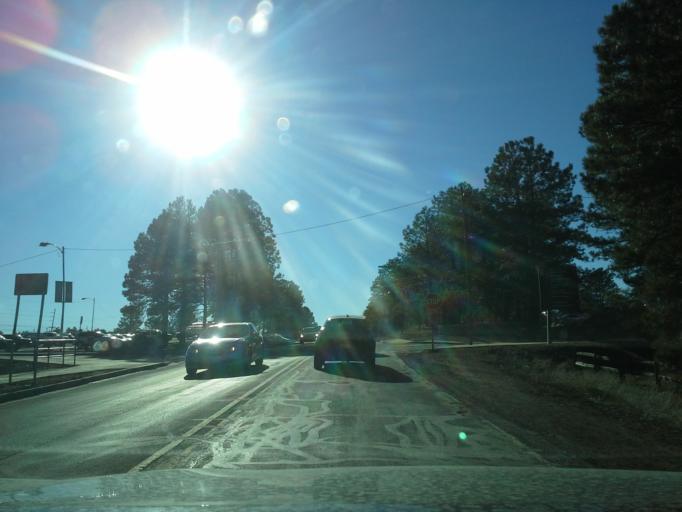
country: US
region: Arizona
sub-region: Coconino County
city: Flagstaff
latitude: 35.1789
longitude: -111.6501
